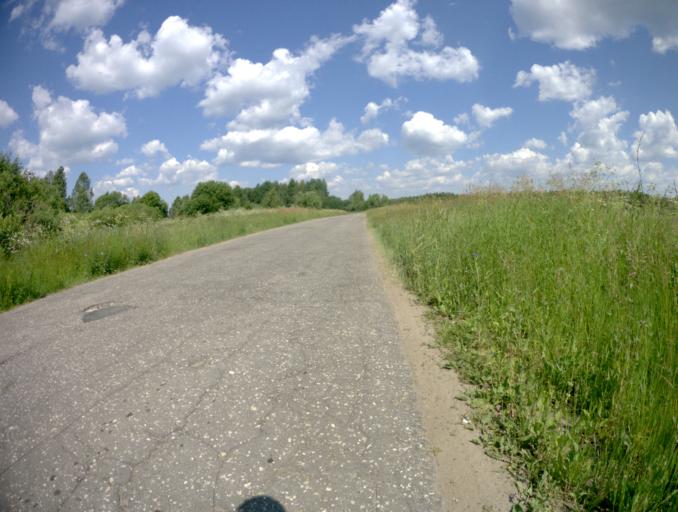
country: RU
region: Vladimir
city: Vyazniki
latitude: 56.3168
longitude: 42.1262
